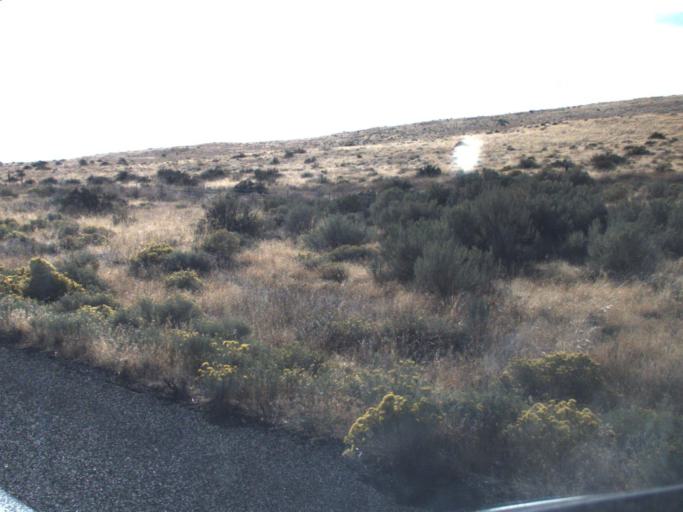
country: US
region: Oregon
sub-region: Morrow County
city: Boardman
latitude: 45.8481
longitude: -119.8672
